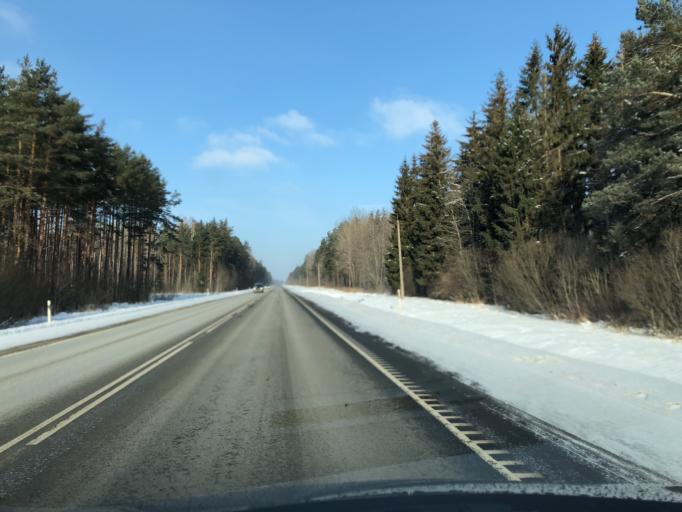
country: EE
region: Tartu
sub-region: Tartu linn
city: Tartu
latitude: 58.3887
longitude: 26.6677
